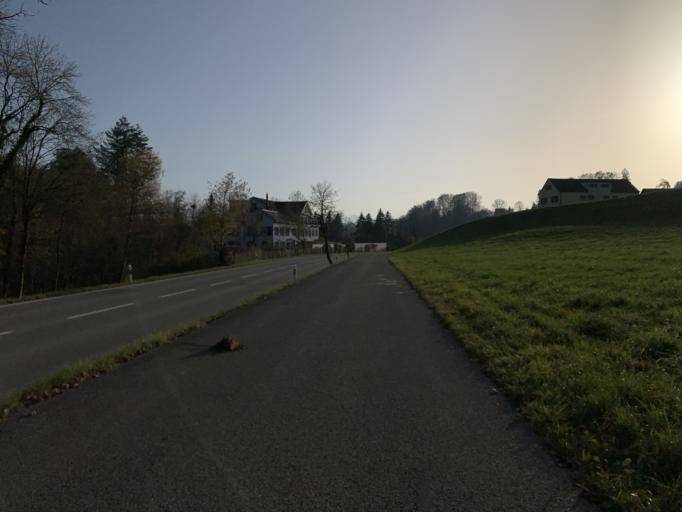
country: CH
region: Zurich
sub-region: Bezirk Hinwil
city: Wald
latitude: 47.2886
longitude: 8.9165
